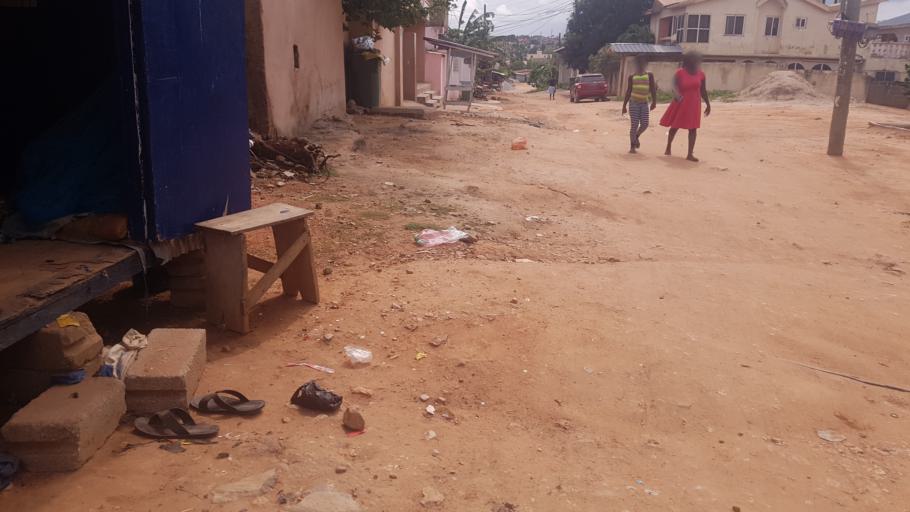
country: GH
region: Greater Accra
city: Gbawe
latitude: 5.5498
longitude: -0.3474
